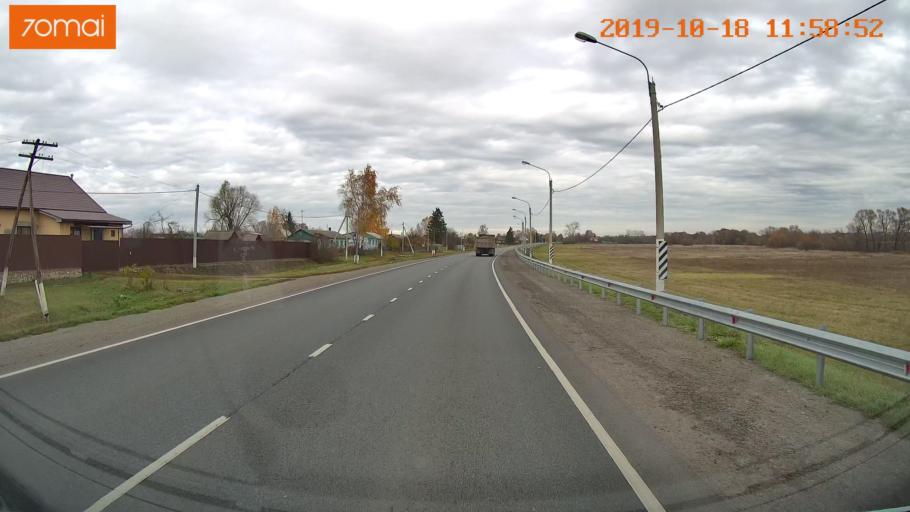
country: RU
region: Rjazan
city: Zakharovo
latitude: 54.2761
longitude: 39.1703
